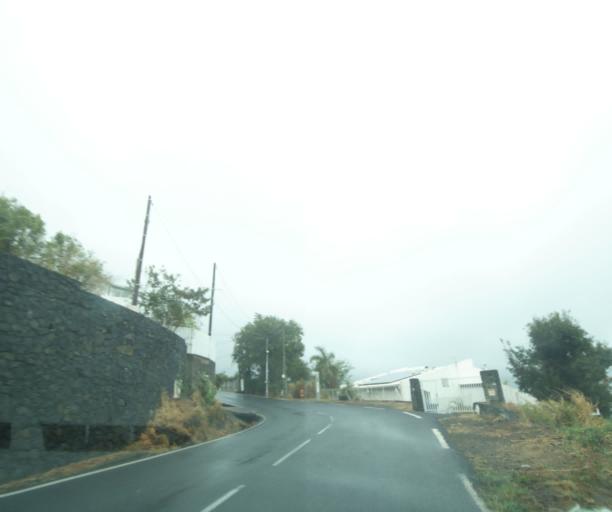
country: RE
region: Reunion
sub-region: Reunion
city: Saint-Paul
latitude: -21.0183
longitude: 55.2882
